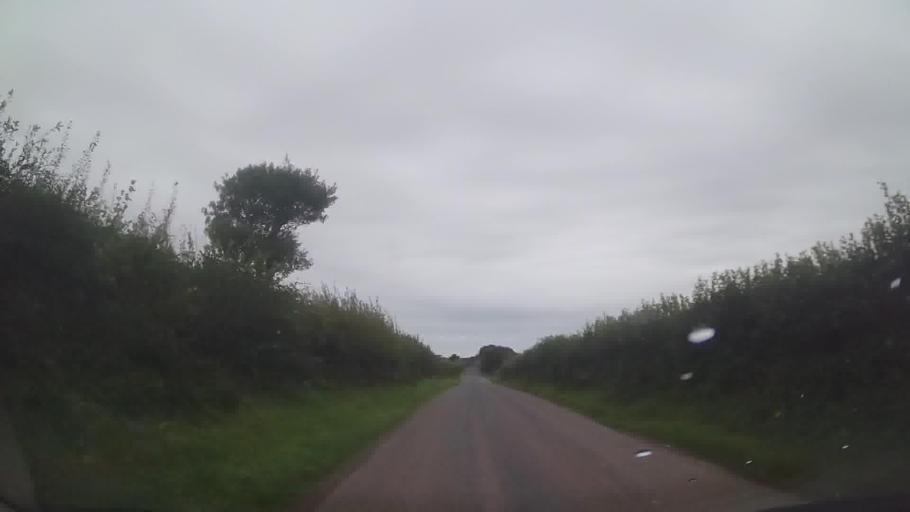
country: GB
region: Wales
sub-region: Carmarthenshire
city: Whitland
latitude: 51.7441
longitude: -4.6222
